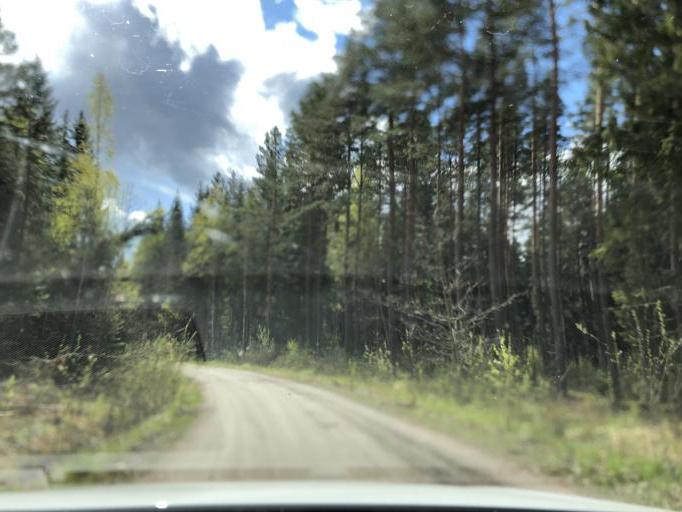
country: SE
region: Uppsala
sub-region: Heby Kommun
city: Tarnsjo
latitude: 60.2629
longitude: 16.9141
